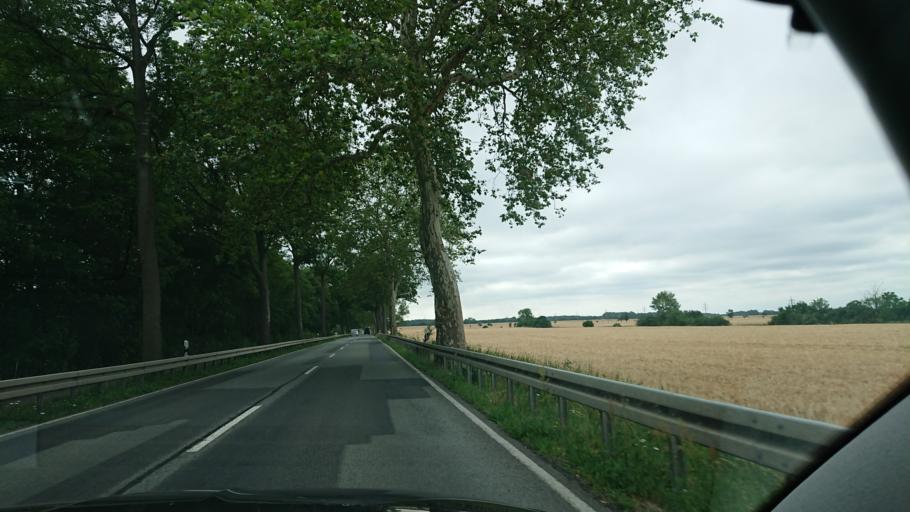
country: DE
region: Brandenburg
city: Perleberg
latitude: 53.0451
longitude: 11.9380
